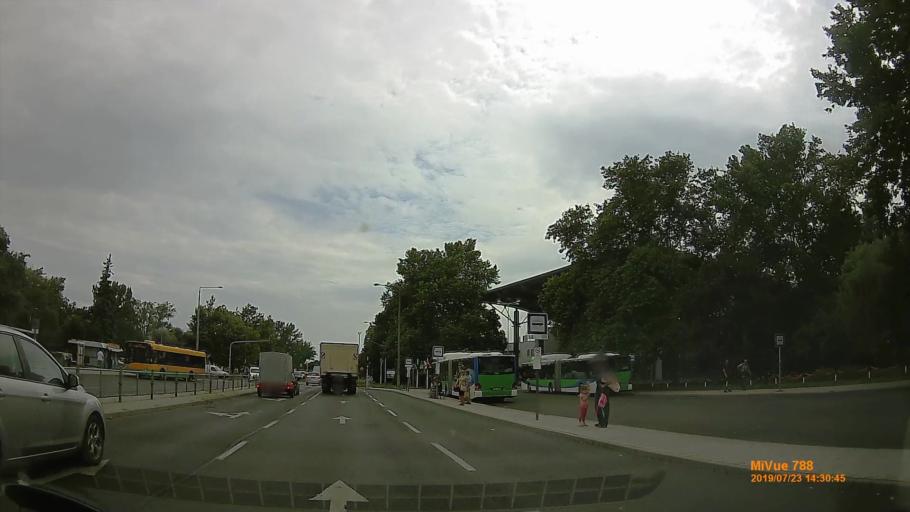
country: HU
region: Szabolcs-Szatmar-Bereg
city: Nyiregyhaza
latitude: 47.9475
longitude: 21.7063
